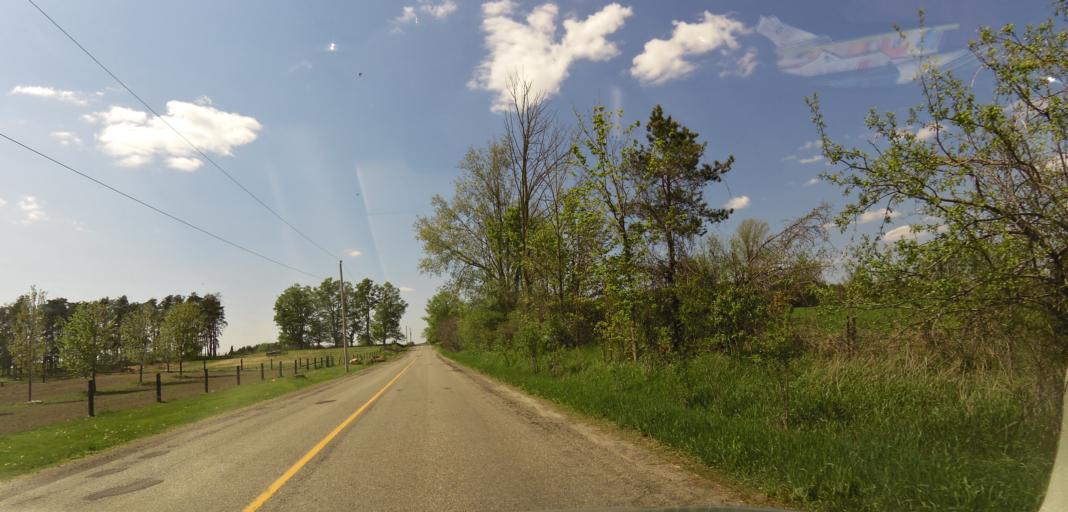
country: CA
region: Ontario
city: Brampton
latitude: 43.8410
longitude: -79.8741
